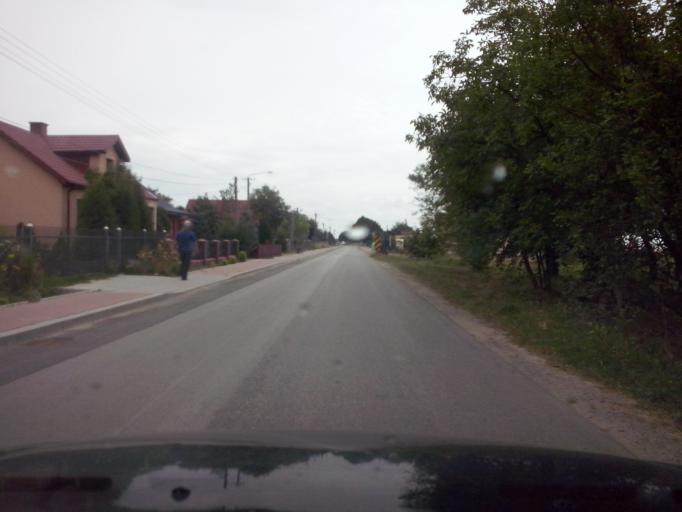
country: PL
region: Swietokrzyskie
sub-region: Powiat kielecki
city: Lagow
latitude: 50.7312
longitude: 21.0976
